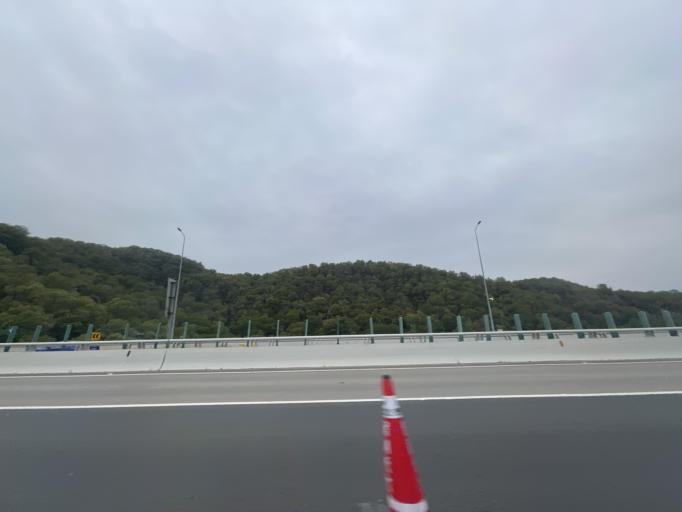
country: CN
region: Guangdong
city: Xinwan
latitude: 22.8035
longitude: 113.6268
